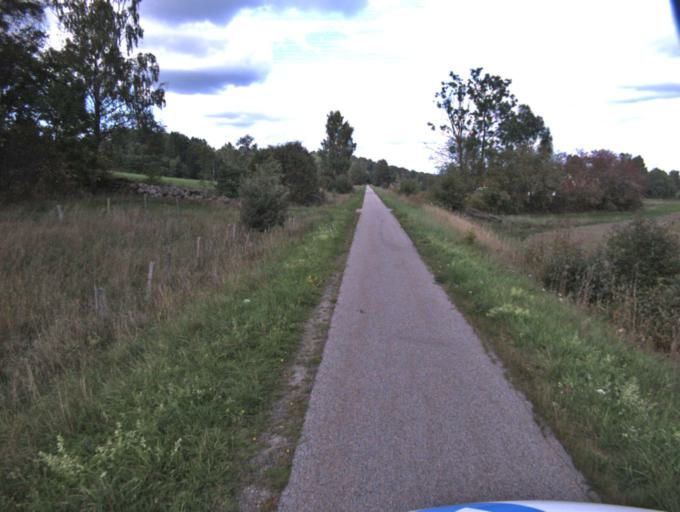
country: SE
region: Vaestra Goetaland
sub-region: Ulricehamns Kommun
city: Ulricehamn
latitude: 57.8826
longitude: 13.4314
